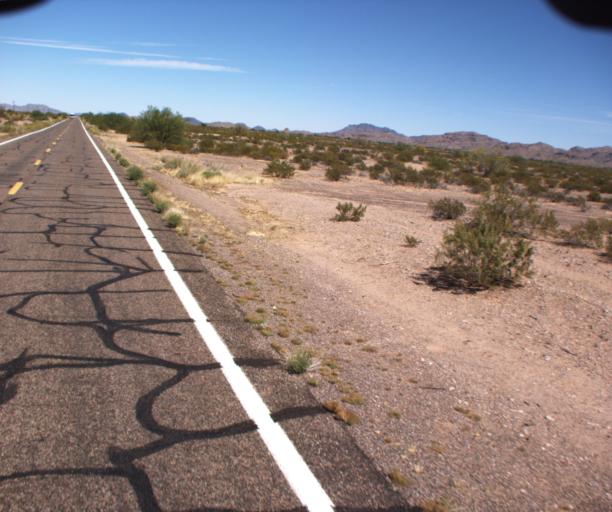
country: US
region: Arizona
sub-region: Pima County
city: Ajo
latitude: 32.6332
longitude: -112.8644
